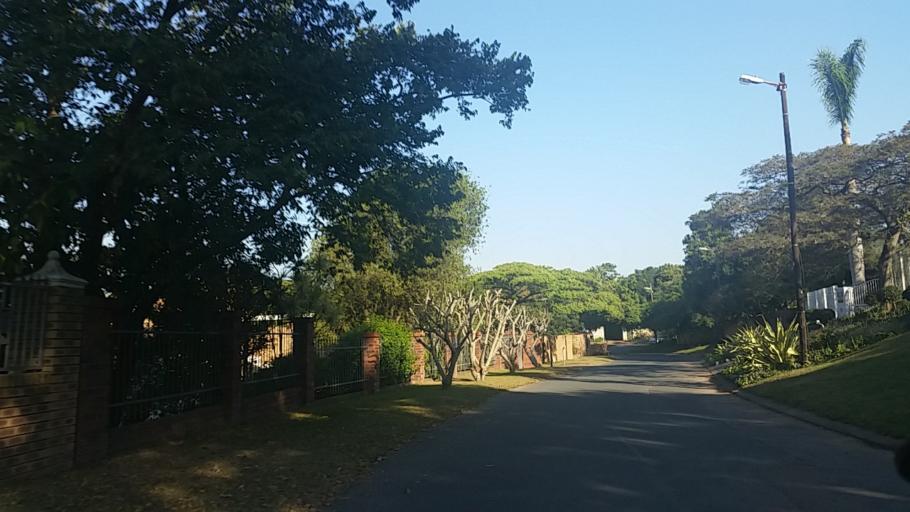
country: ZA
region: KwaZulu-Natal
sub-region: eThekwini Metropolitan Municipality
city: Berea
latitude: -29.8469
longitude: 30.9042
